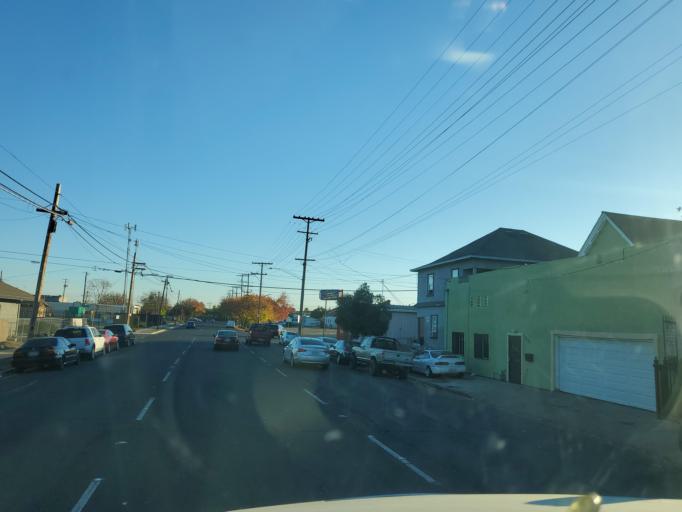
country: US
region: California
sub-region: San Joaquin County
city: Stockton
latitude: 37.9412
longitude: -121.2880
